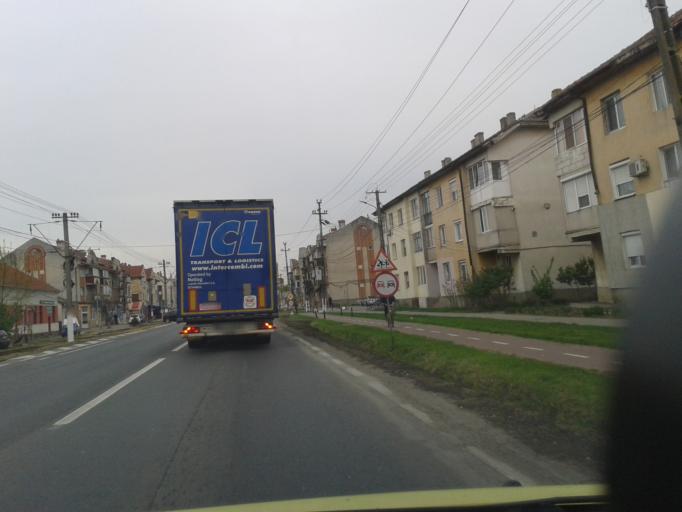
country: RO
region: Arad
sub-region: Comuna Vladimirescu
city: Vladimirescu
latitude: 46.1644
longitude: 21.4018
